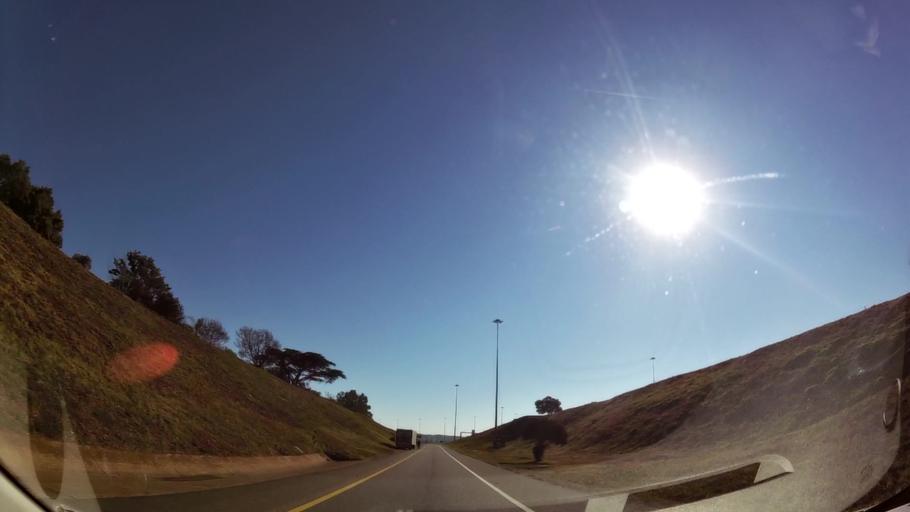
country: ZA
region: Gauteng
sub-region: City of Tshwane Metropolitan Municipality
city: Centurion
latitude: -25.8295
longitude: 28.2416
